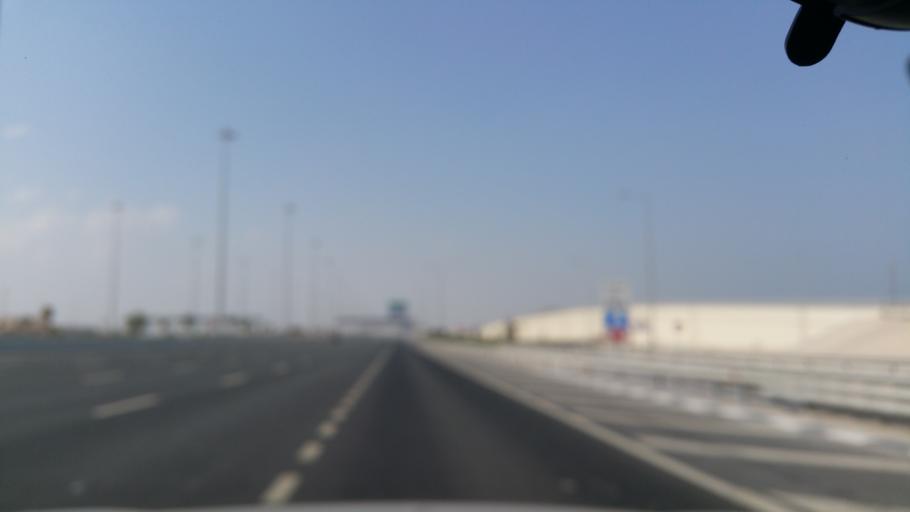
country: QA
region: Baladiyat Umm Salal
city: Umm Salal Muhammad
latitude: 25.4451
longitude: 51.4812
